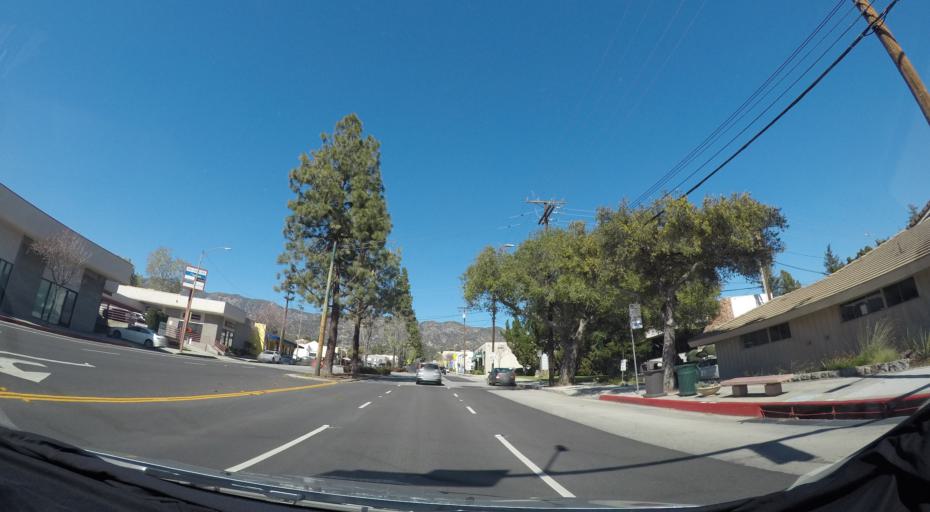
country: US
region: California
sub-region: Los Angeles County
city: La Crescenta-Montrose
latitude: 34.2009
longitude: -118.2279
